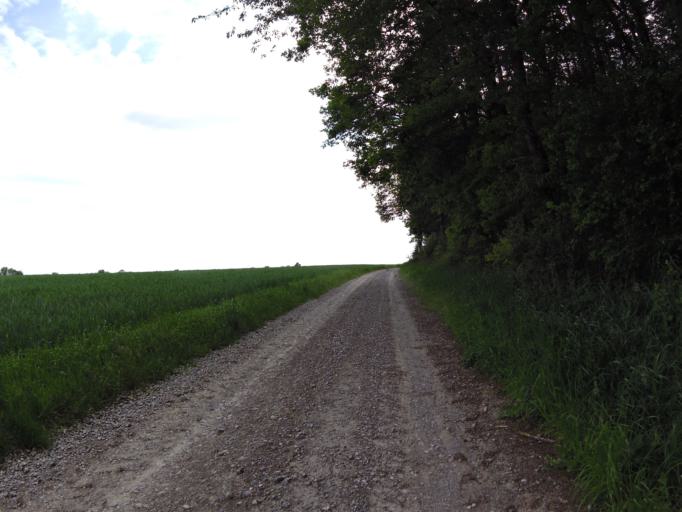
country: DE
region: Bavaria
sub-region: Regierungsbezirk Unterfranken
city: Biebelried
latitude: 49.7276
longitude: 10.0688
